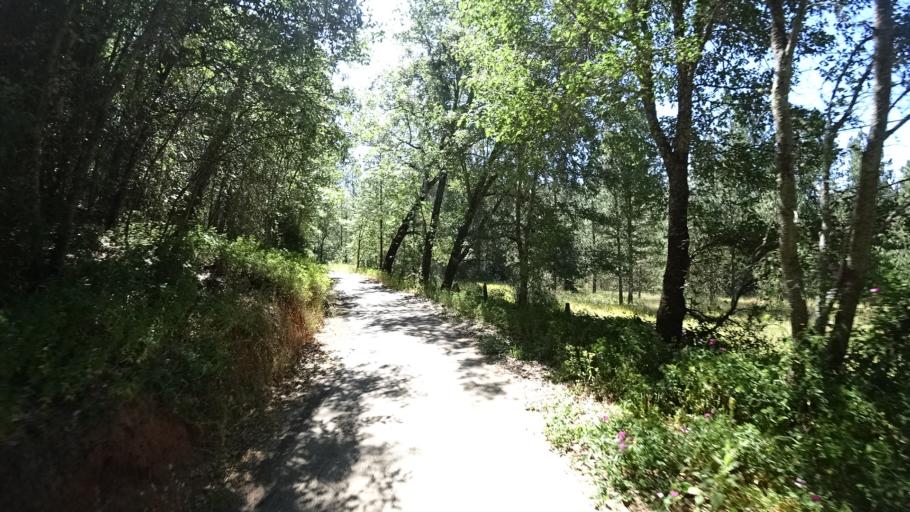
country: US
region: California
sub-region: Amador County
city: Pioneer
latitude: 38.3863
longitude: -120.4972
